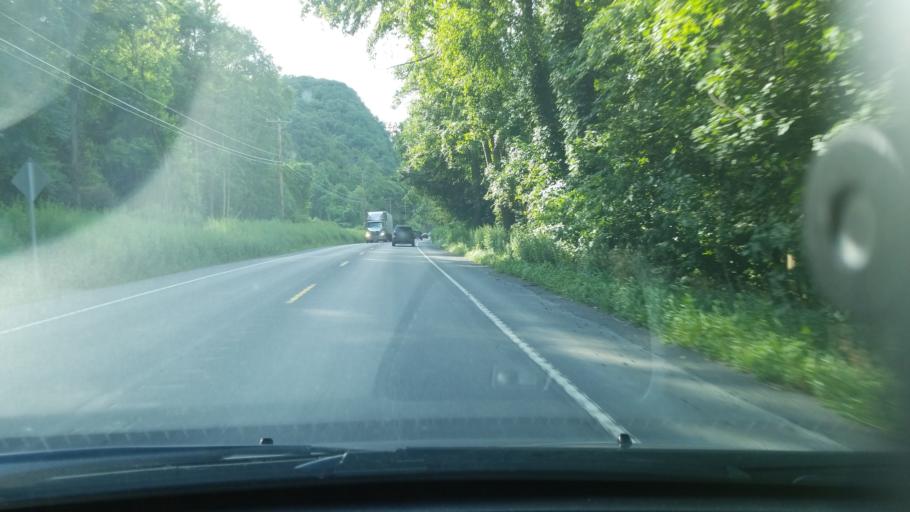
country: US
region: Pennsylvania
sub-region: Montour County
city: Danville
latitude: 40.9403
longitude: -76.6039
